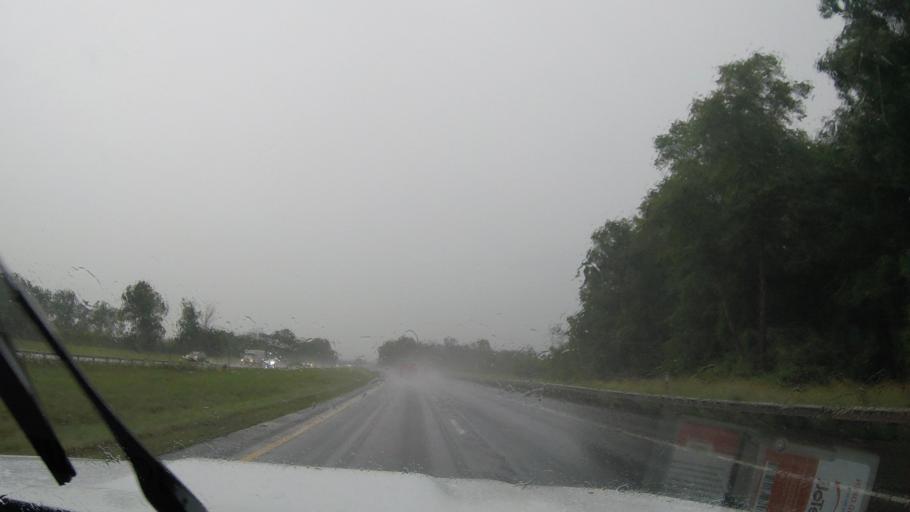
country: US
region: New York
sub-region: Seneca County
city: Seneca Falls
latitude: 42.9746
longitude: -76.8079
